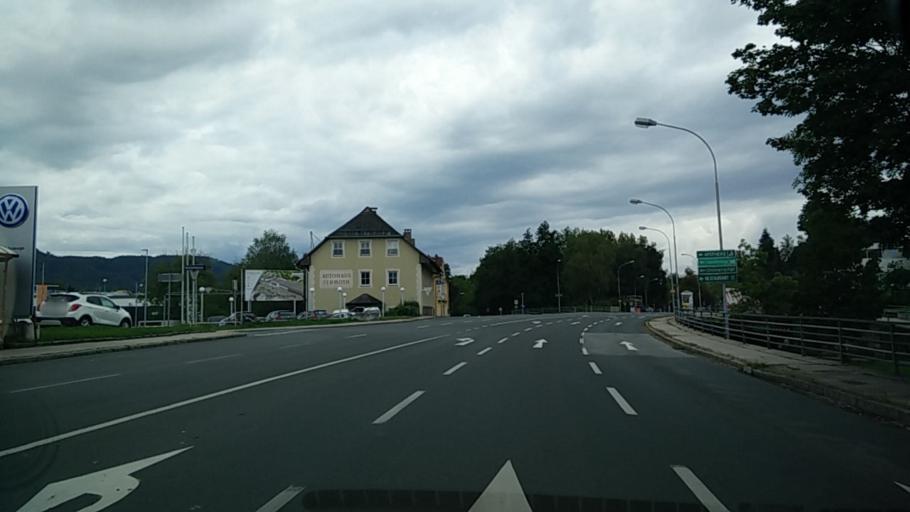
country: AT
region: Carinthia
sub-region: Klagenfurt am Woerthersee
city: Klagenfurt am Woerthersee
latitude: 46.6197
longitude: 14.2719
